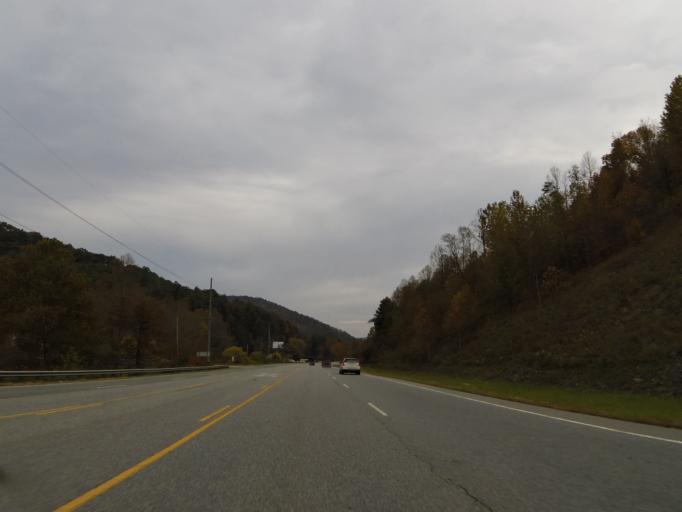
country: US
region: North Carolina
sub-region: Caldwell County
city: Lenoir
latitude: 36.0244
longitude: -81.5779
